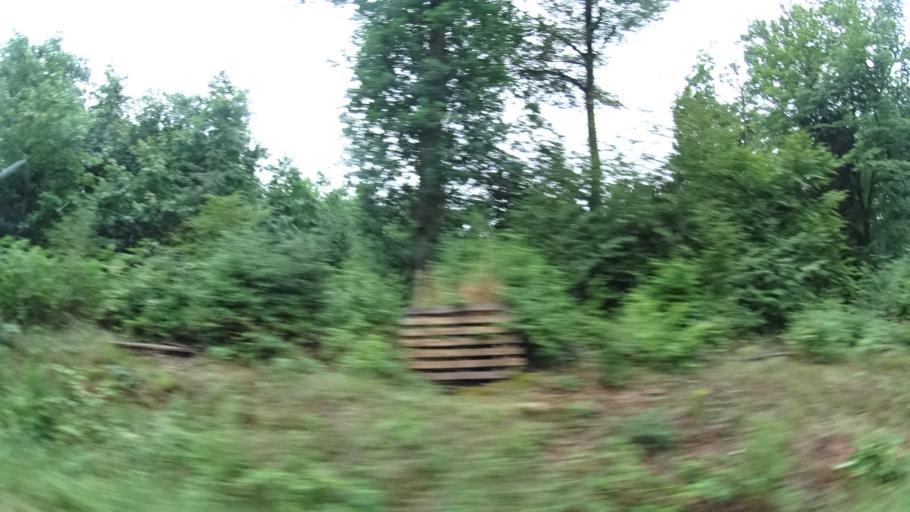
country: BE
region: Wallonia
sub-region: Province du Luxembourg
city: Daverdisse
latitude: 49.9640
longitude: 5.1113
